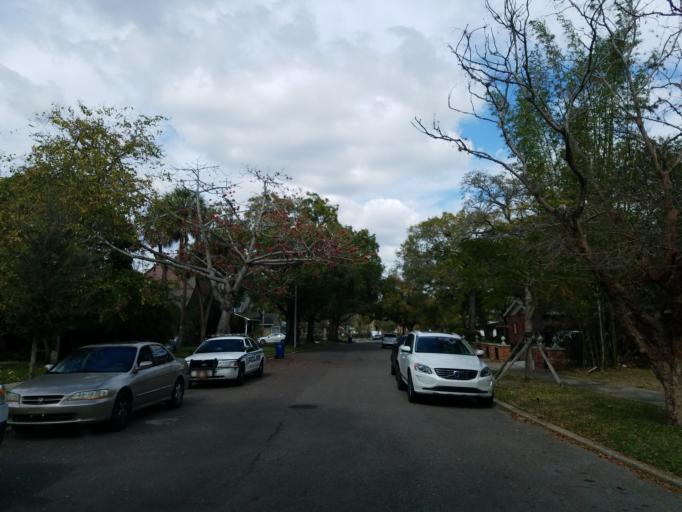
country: US
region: Florida
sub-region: Hillsborough County
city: Tampa
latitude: 27.9274
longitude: -82.4569
